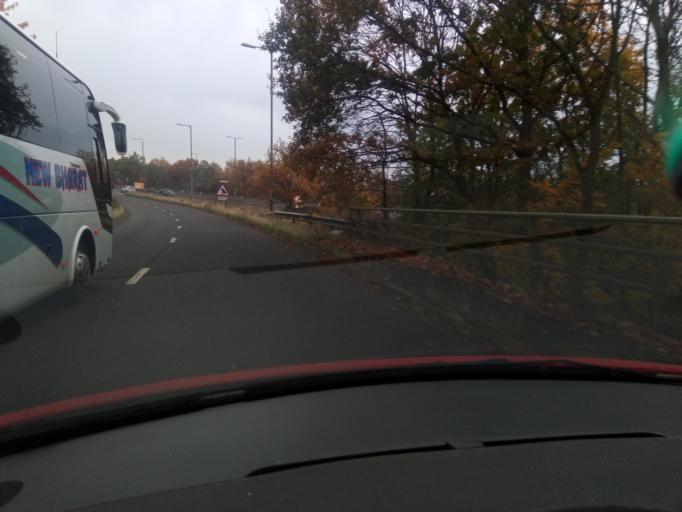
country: GB
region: England
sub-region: Derbyshire
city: Borrowash
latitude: 52.9157
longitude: -1.4188
